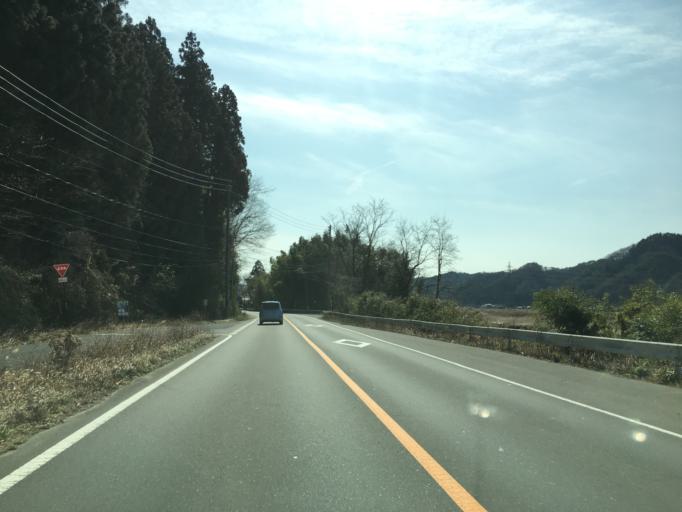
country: JP
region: Ibaraki
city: Daigo
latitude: 36.9286
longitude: 140.4152
